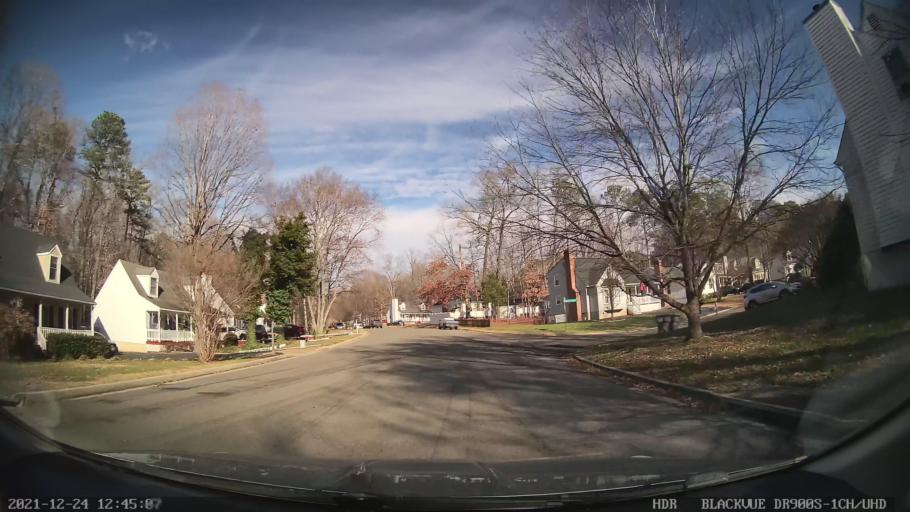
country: US
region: Virginia
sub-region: Henrico County
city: Short Pump
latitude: 37.6287
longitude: -77.6269
